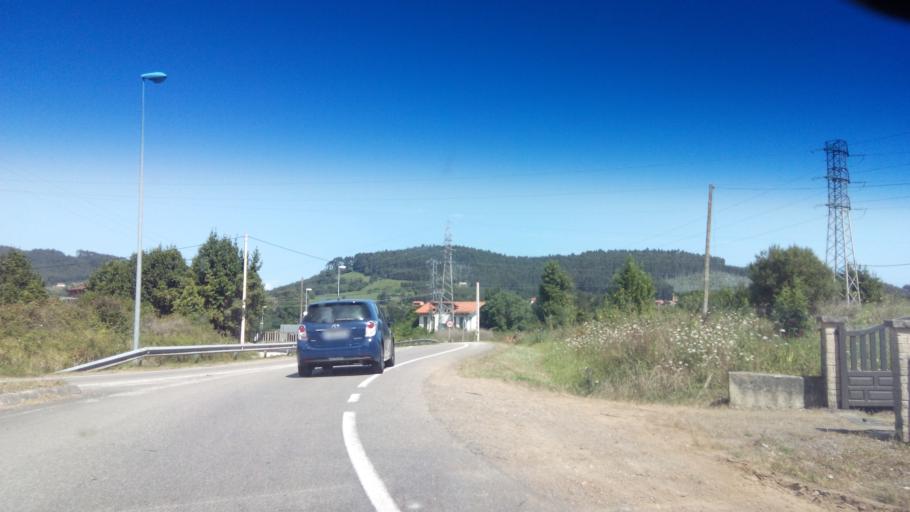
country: ES
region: Asturias
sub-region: Province of Asturias
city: Colunga
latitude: 43.4809
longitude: -5.2546
